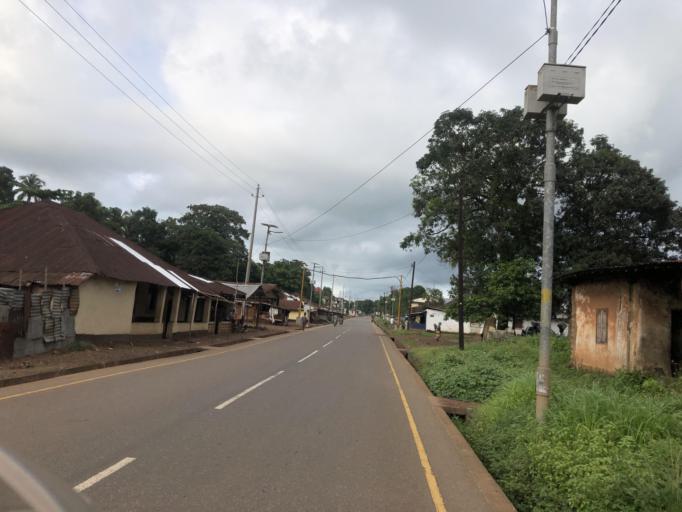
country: SL
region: Northern Province
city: Port Loko
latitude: 8.7669
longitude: -12.7846
